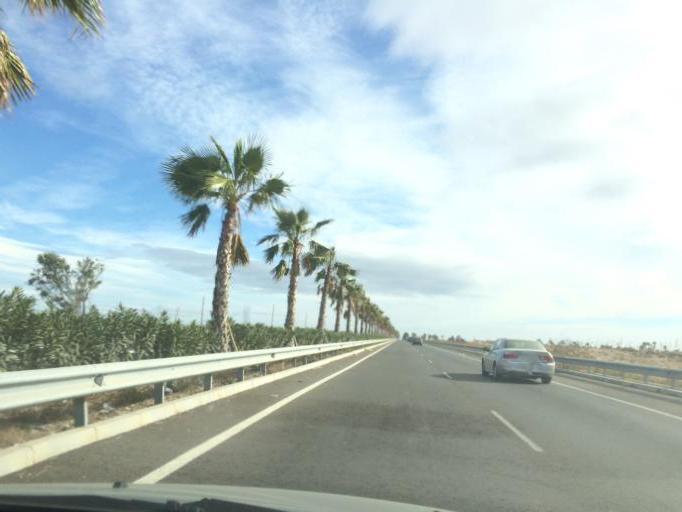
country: ES
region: Andalusia
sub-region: Provincia de Almeria
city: Retamar
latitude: 36.8521
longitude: -2.3274
